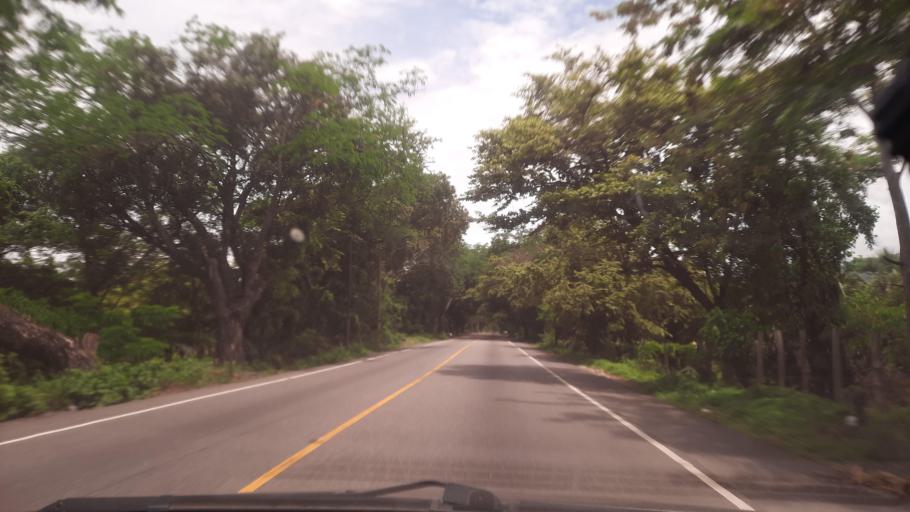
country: GT
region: Zacapa
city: Rio Hondo
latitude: 15.0670
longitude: -89.5217
